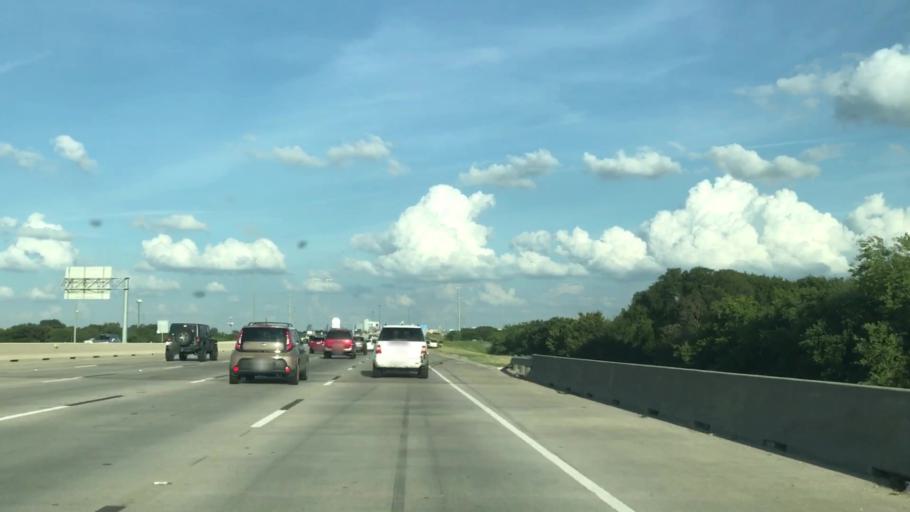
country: US
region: Texas
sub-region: Dallas County
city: Cockrell Hill
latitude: 32.7654
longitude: -96.9263
